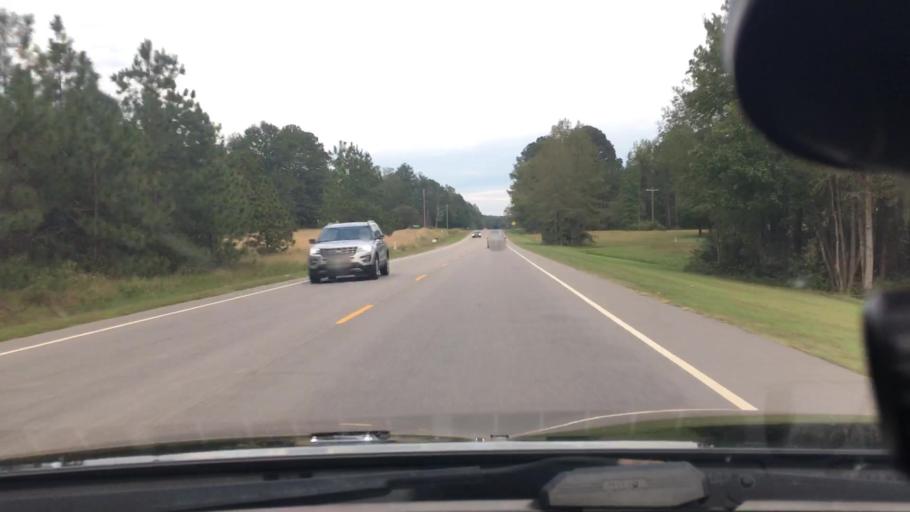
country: US
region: North Carolina
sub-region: Lee County
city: Sanford
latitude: 35.3898
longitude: -79.2608
